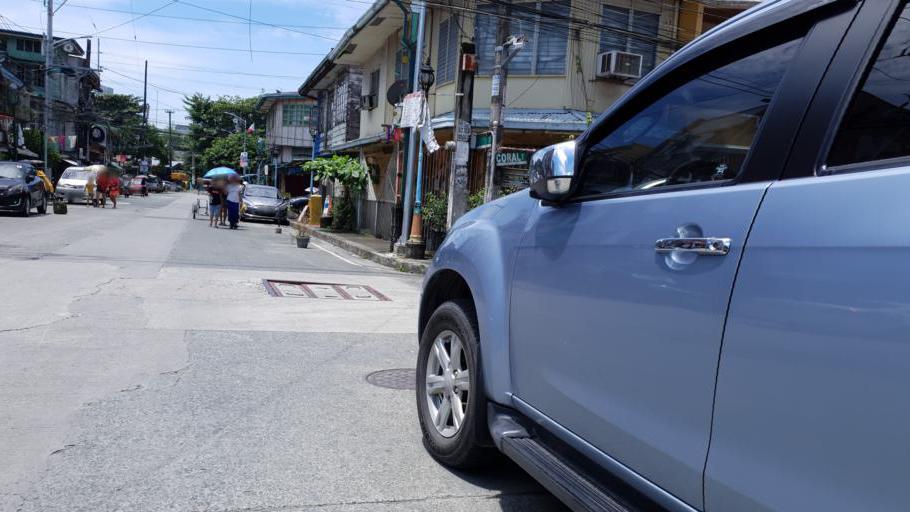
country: PH
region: Metro Manila
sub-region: City of Manila
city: Quiapo
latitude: 14.5719
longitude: 121.0017
